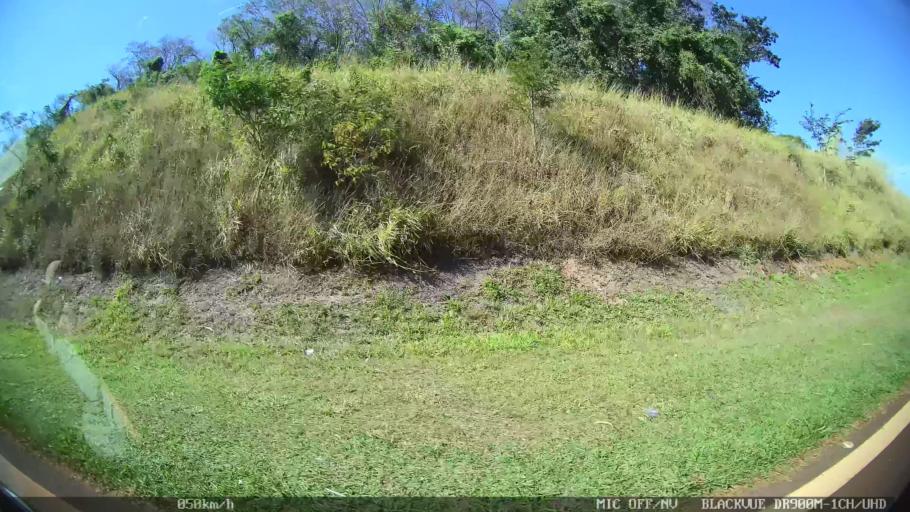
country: BR
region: Sao Paulo
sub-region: Franca
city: Franca
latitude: -20.6333
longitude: -47.4680
